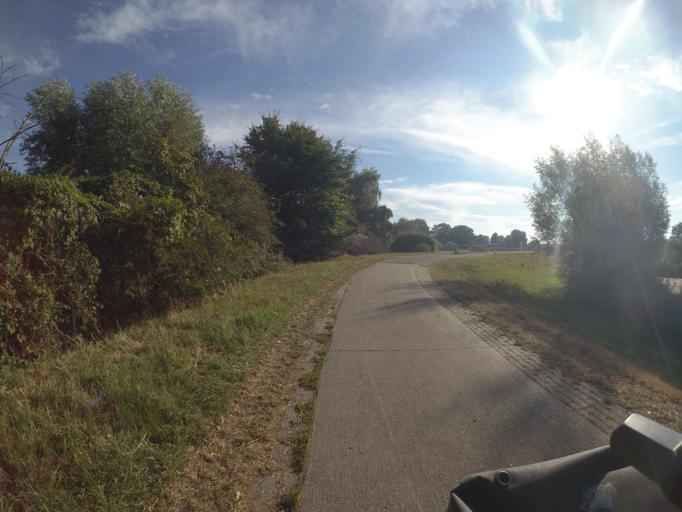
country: NL
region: Overijssel
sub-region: Gemeente Zwartewaterland
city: Hasselt
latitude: 52.5608
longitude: 6.1130
